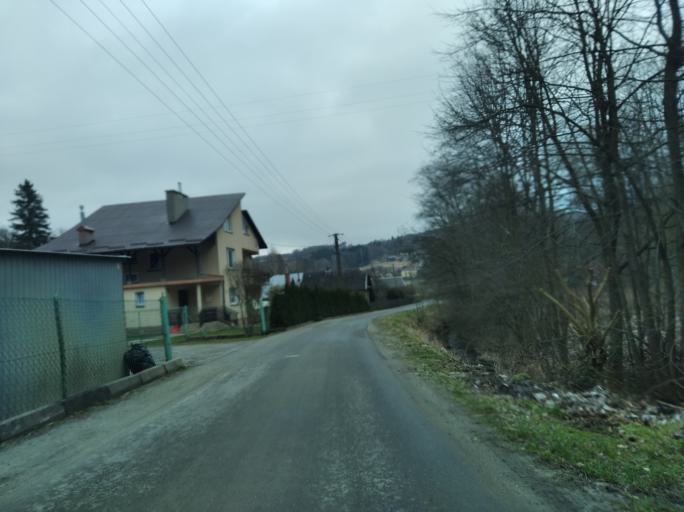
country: PL
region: Subcarpathian Voivodeship
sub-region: Powiat strzyzowski
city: Strzyzow
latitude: 49.8922
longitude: 21.8211
